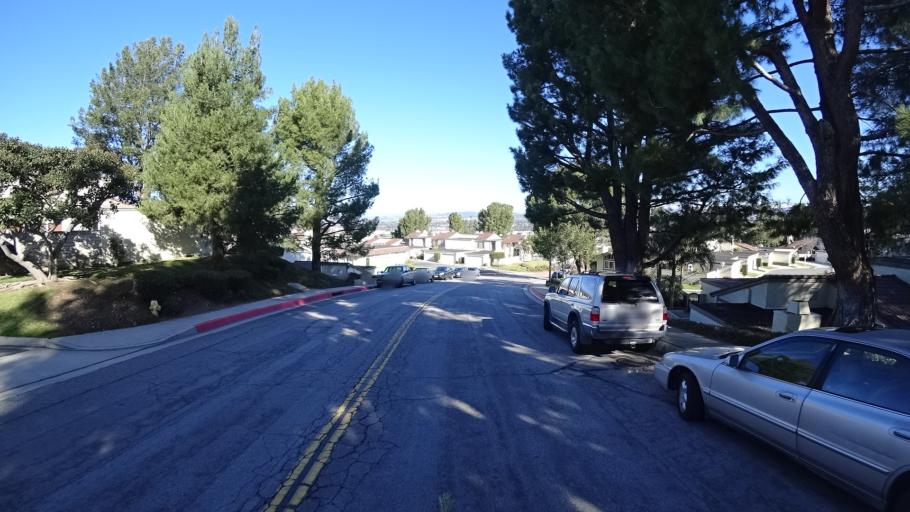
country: US
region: California
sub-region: Orange County
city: Villa Park
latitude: 33.8475
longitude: -117.7931
